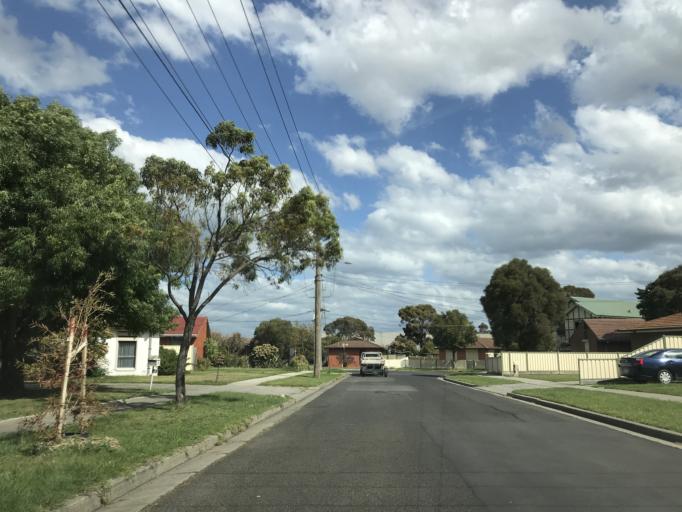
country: AU
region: Victoria
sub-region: Brimbank
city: Sunshine West
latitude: -37.8024
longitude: 144.8143
